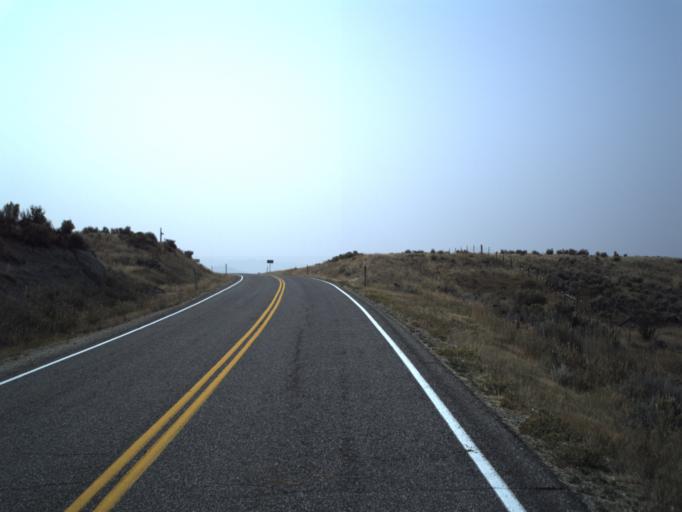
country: US
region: Utah
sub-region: Morgan County
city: Morgan
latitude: 40.9558
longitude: -111.5493
